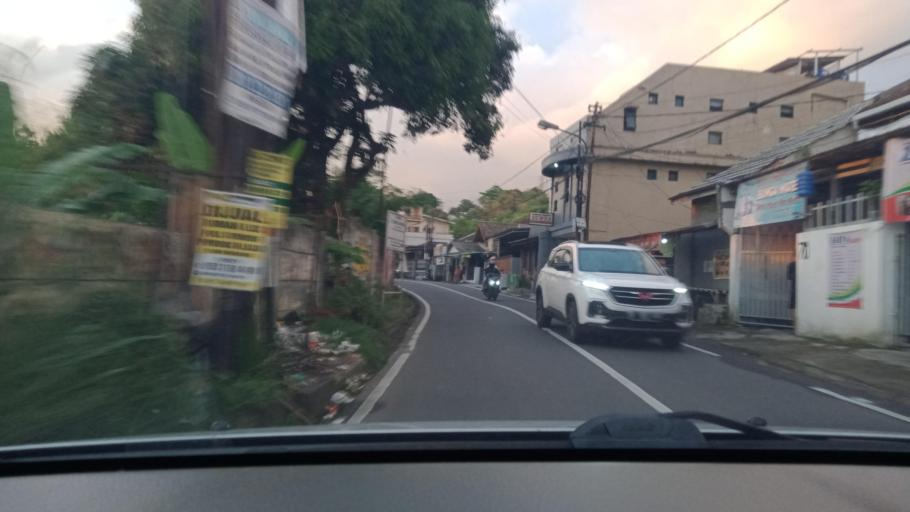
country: ID
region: West Java
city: Lembang
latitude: -6.8535
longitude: 107.5916
